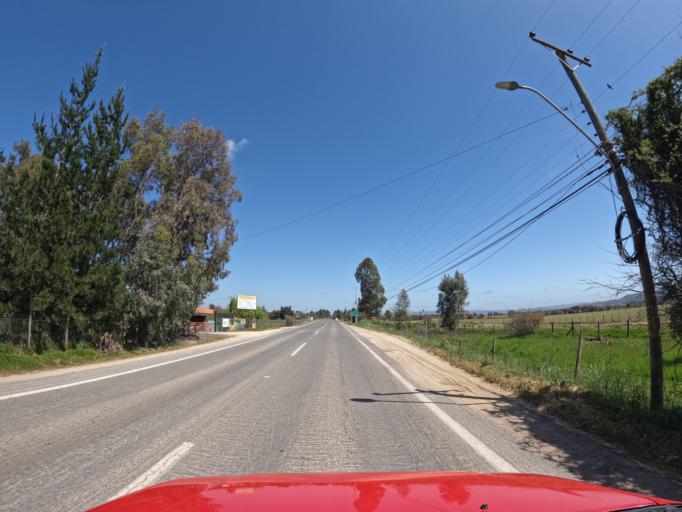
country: CL
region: O'Higgins
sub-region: Provincia de Colchagua
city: Santa Cruz
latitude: -34.7297
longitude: -71.6714
